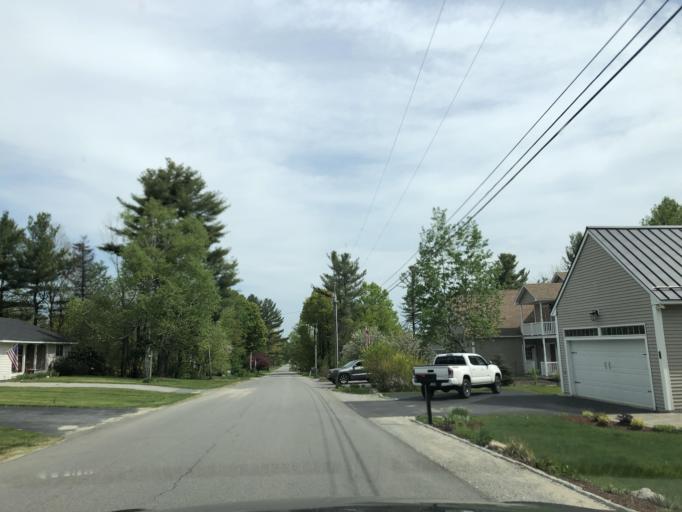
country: US
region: New Hampshire
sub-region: Merrimack County
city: New London
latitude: 43.4202
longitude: -71.9946
